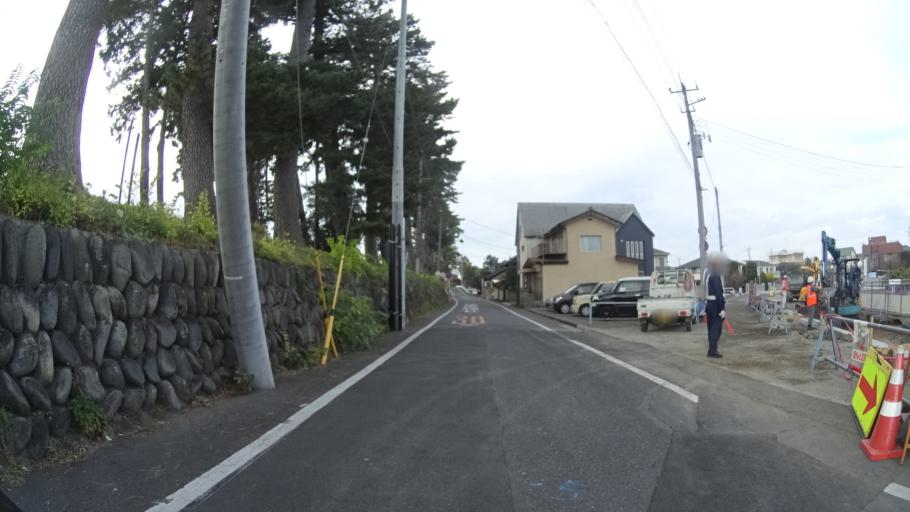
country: JP
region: Gunma
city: Maebashi-shi
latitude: 36.3961
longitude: 139.0626
